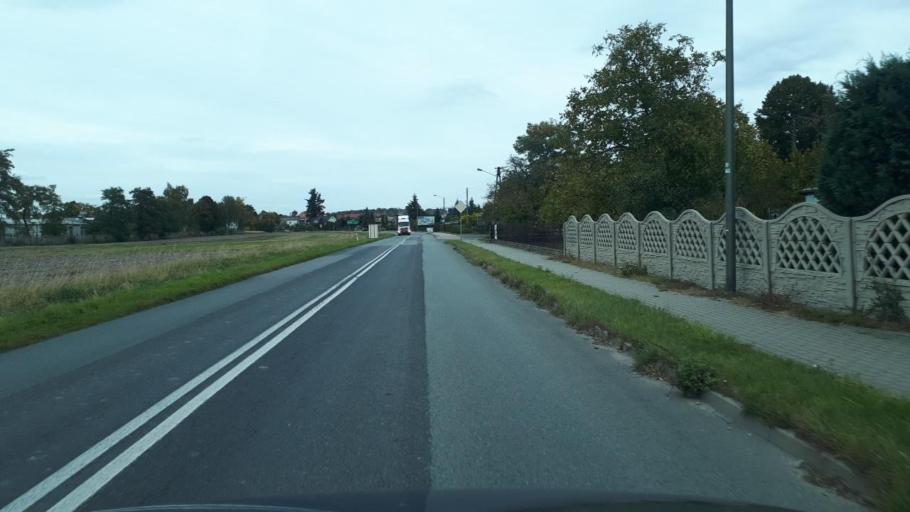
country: PL
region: Opole Voivodeship
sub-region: Powiat oleski
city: Dobrodzien
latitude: 50.7151
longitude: 18.4468
